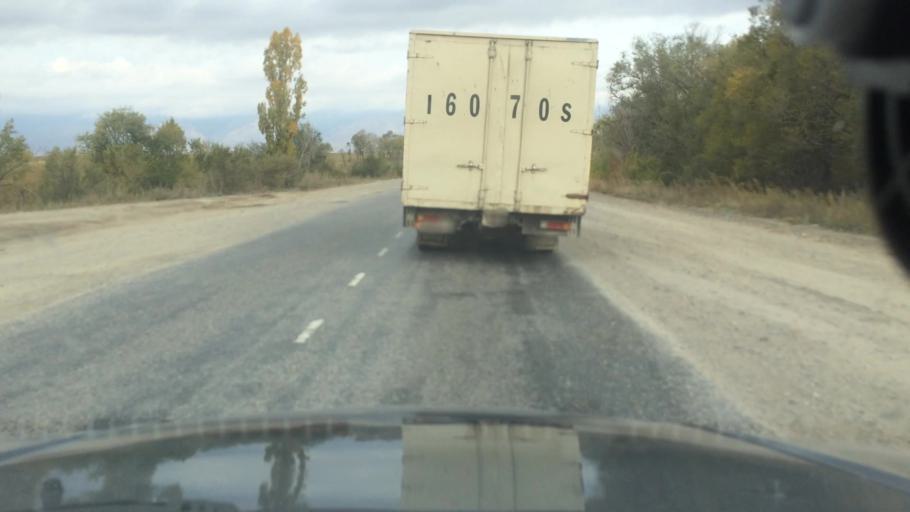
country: KG
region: Ysyk-Koel
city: Tyup
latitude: 42.6668
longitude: 78.3491
